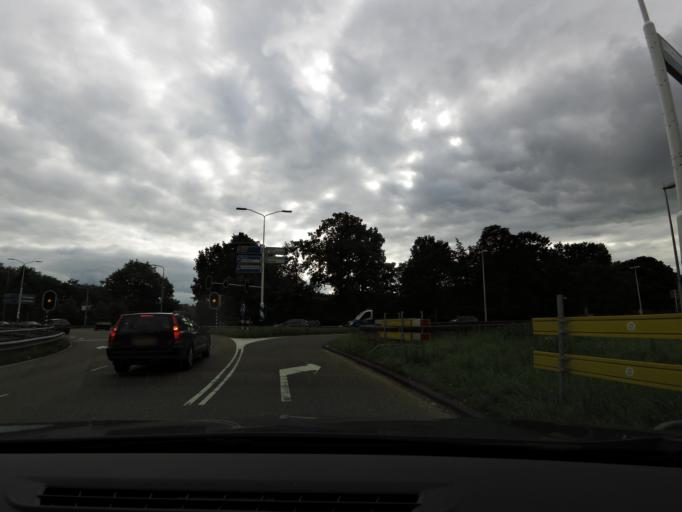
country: NL
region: Utrecht
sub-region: Gemeente Utrecht
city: Utrecht
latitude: 52.0963
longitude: 5.1432
